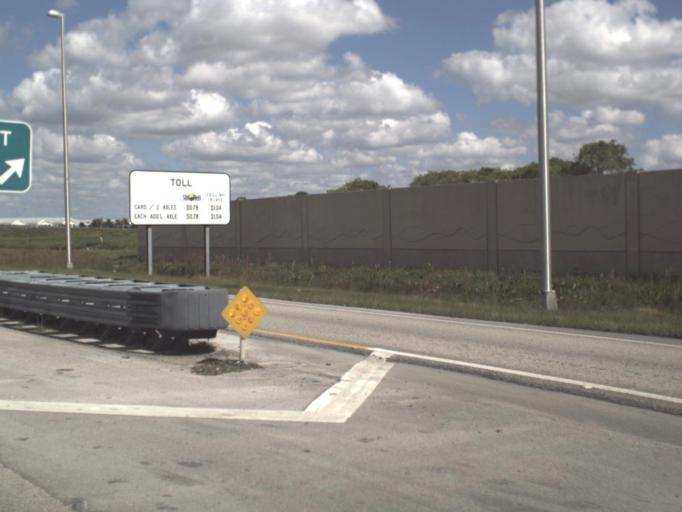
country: US
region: Florida
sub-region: Miami-Dade County
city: Doral
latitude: 25.8366
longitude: -80.3868
